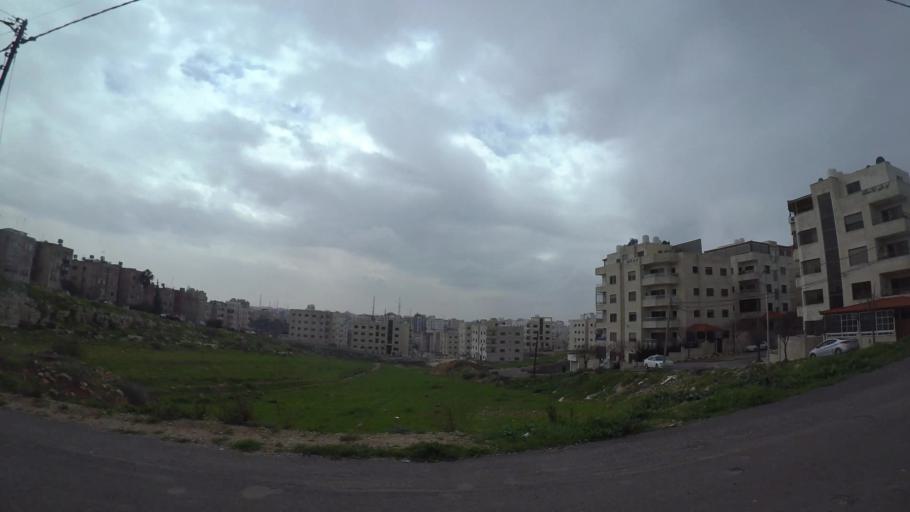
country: JO
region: Amman
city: Umm as Summaq
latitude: 31.9040
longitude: 35.8364
